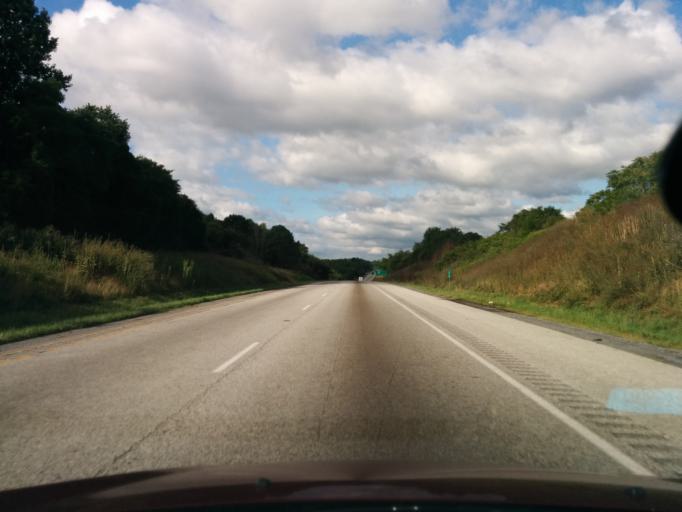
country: US
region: Virginia
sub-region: Rockbridge County
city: Glasgow
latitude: 37.6827
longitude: -79.4920
